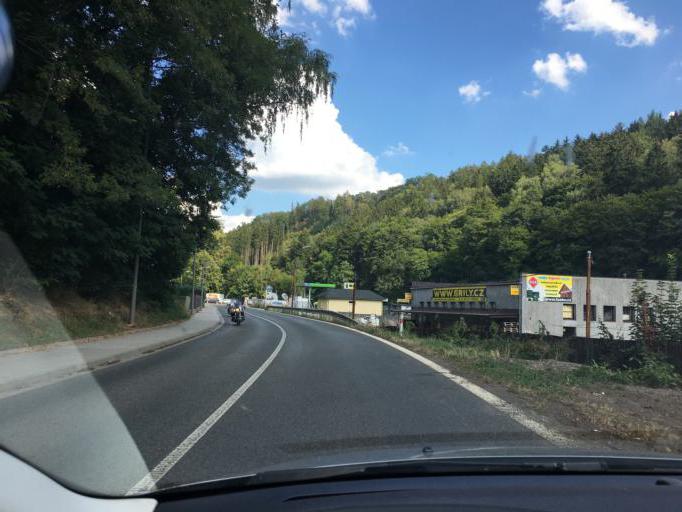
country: CZ
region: Liberecky
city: Semily
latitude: 50.5960
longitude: 15.3442
